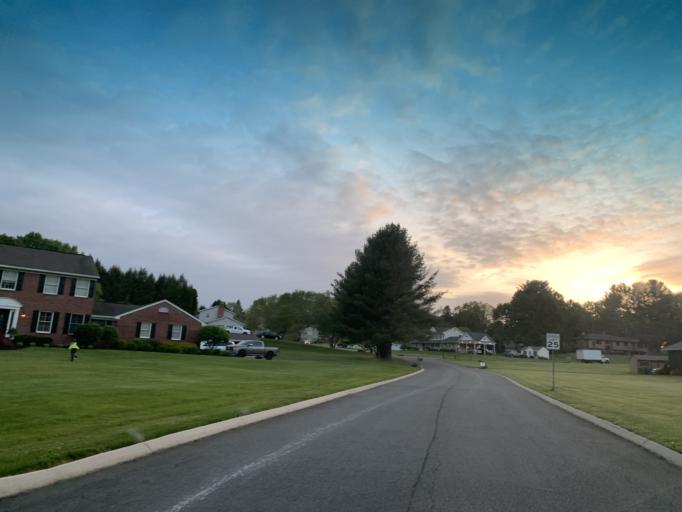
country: US
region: Maryland
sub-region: Harford County
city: South Bel Air
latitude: 39.5882
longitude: -76.2775
